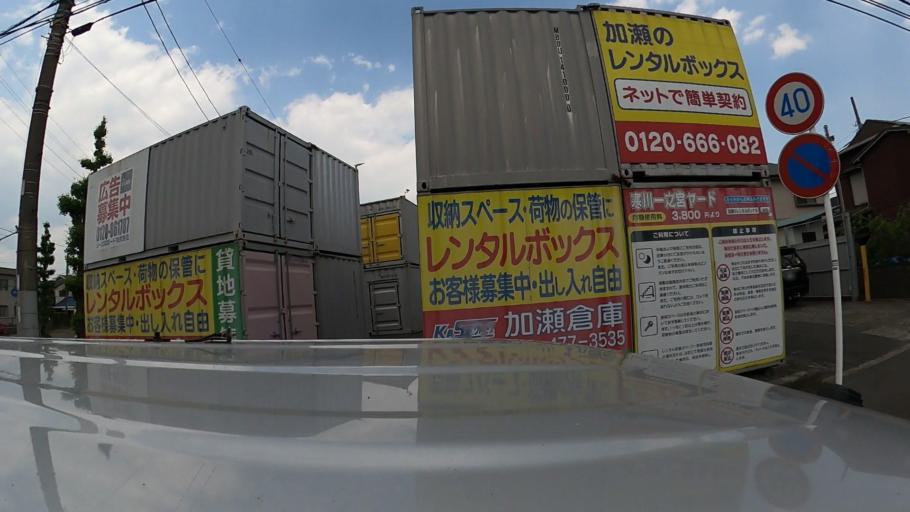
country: JP
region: Kanagawa
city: Chigasaki
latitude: 35.3648
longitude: 139.3814
